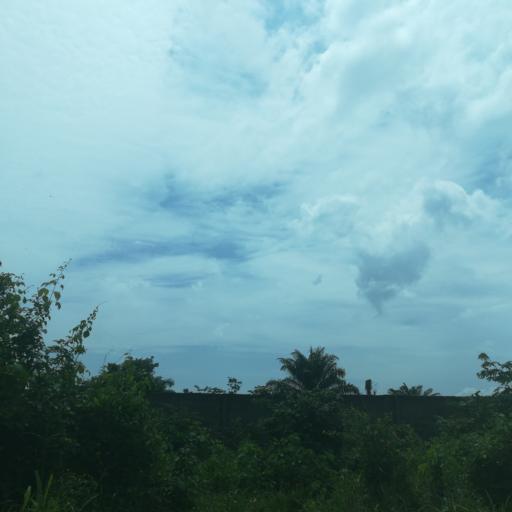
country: NG
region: Lagos
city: Ejirin
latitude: 6.6294
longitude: 3.7079
